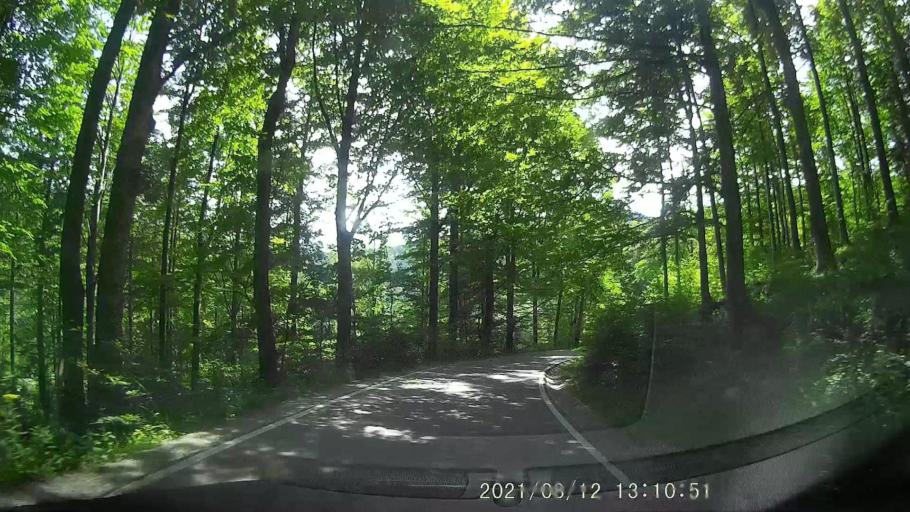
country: PL
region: Lower Silesian Voivodeship
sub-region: Powiat klodzki
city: Stronie Slaskie
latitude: 50.2451
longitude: 16.8504
